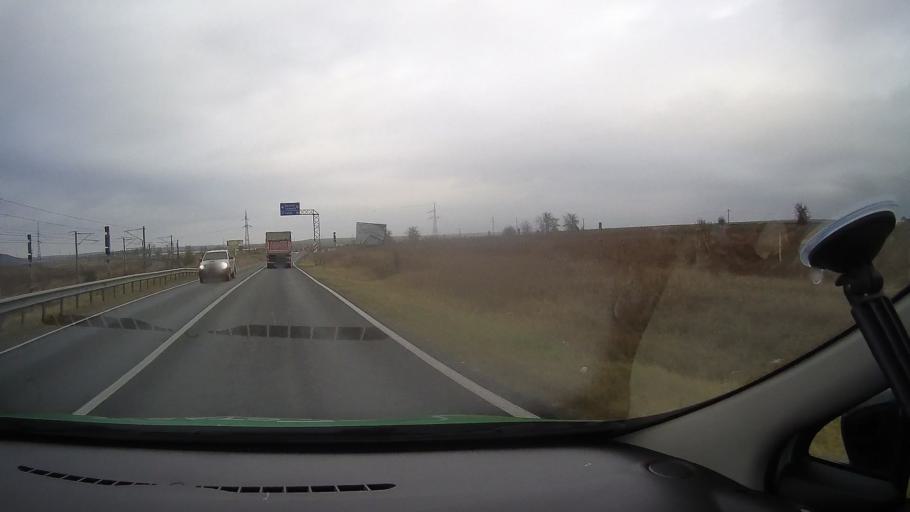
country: RO
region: Constanta
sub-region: Comuna Poarta Alba
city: Poarta Alba
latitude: 44.2318
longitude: 28.3774
